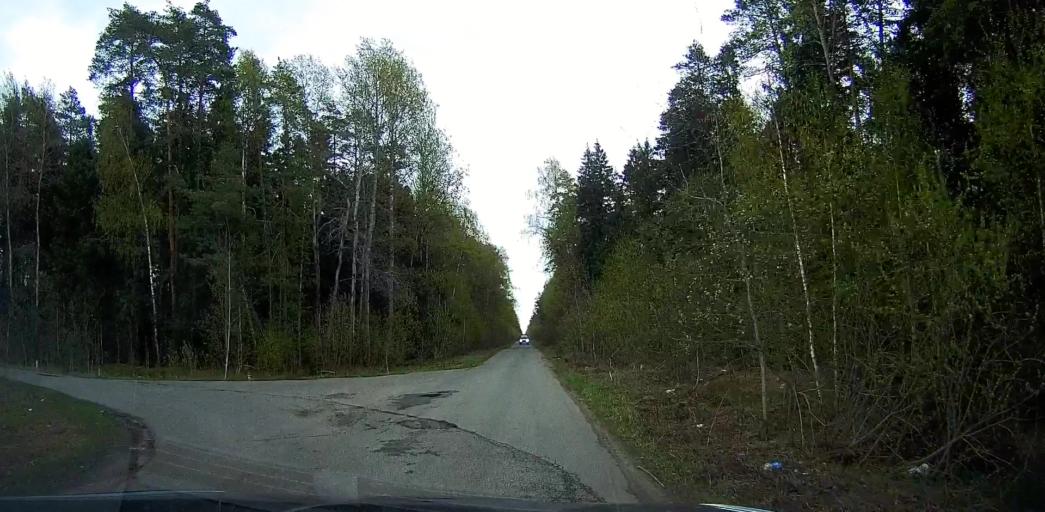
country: RU
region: Moskovskaya
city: Malyshevo
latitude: 55.5508
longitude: 38.3531
